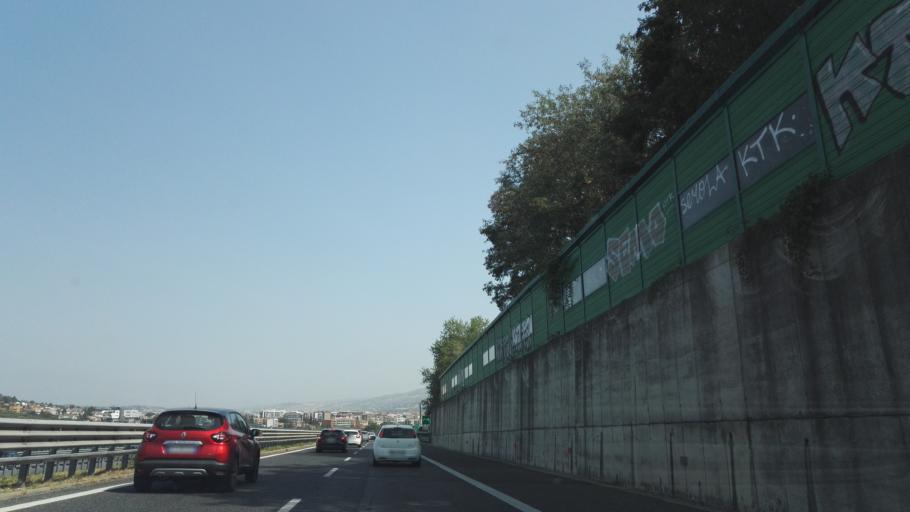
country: IT
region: Calabria
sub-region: Provincia di Cosenza
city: Cosenza
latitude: 39.3098
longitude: 16.2386
